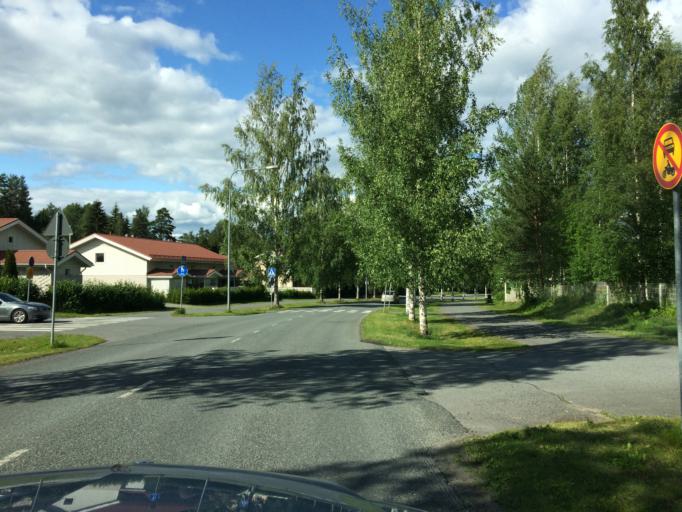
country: FI
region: Haeme
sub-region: Haemeenlinna
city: Parola
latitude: 60.9840
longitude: 24.3831
